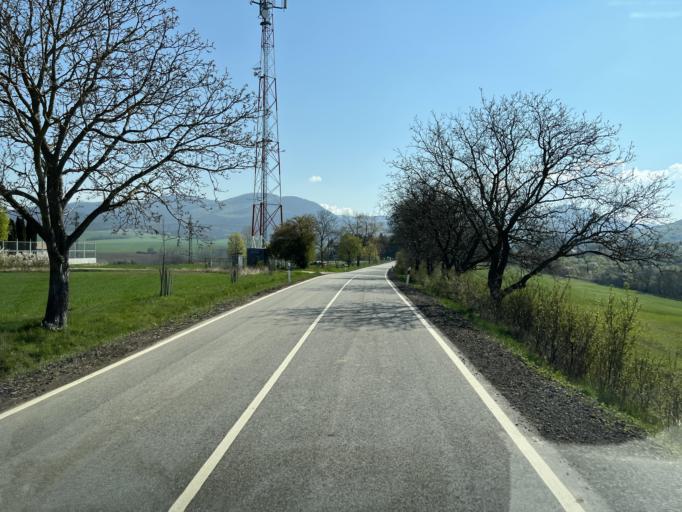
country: HU
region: Pest
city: Szob
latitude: 47.9366
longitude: 18.8121
